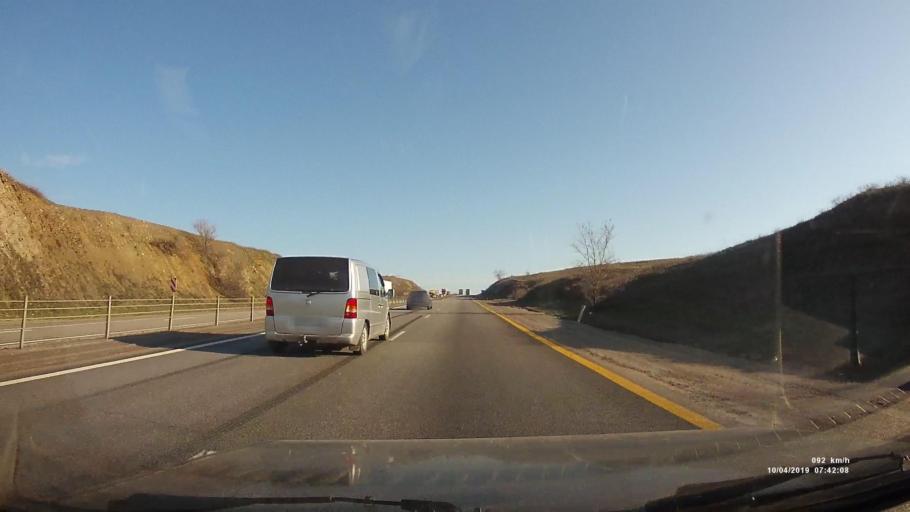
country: RU
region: Rostov
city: Likhoy
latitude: 48.1446
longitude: 40.2600
